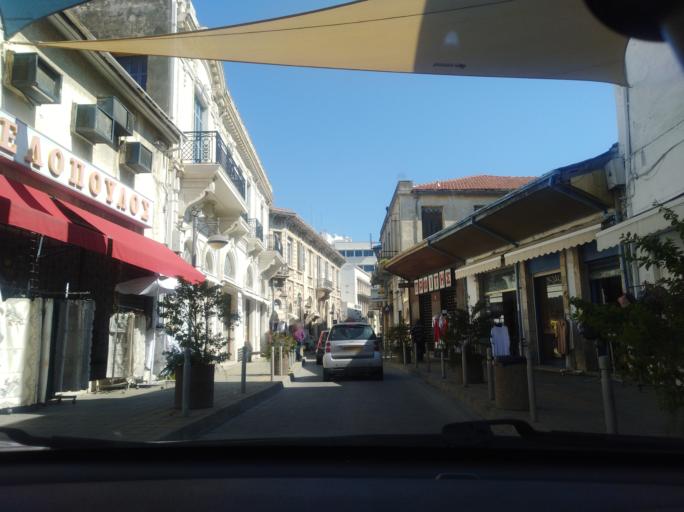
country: CY
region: Limassol
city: Limassol
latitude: 34.6736
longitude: 33.0431
